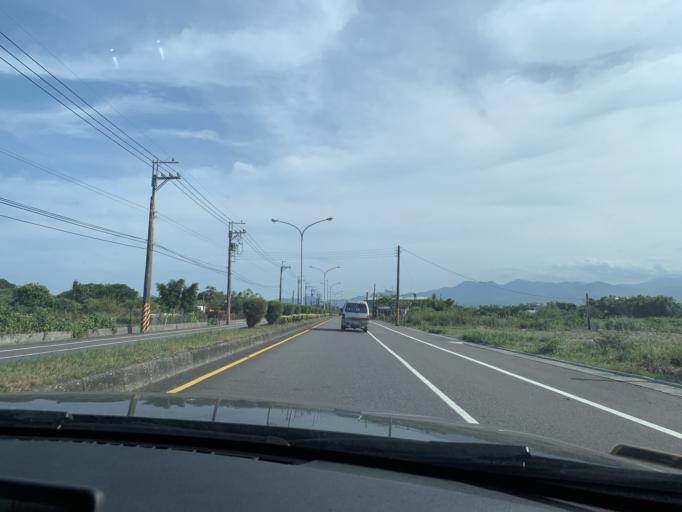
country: TW
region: Taiwan
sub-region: Yilan
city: Yilan
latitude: 24.7431
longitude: 121.8166
